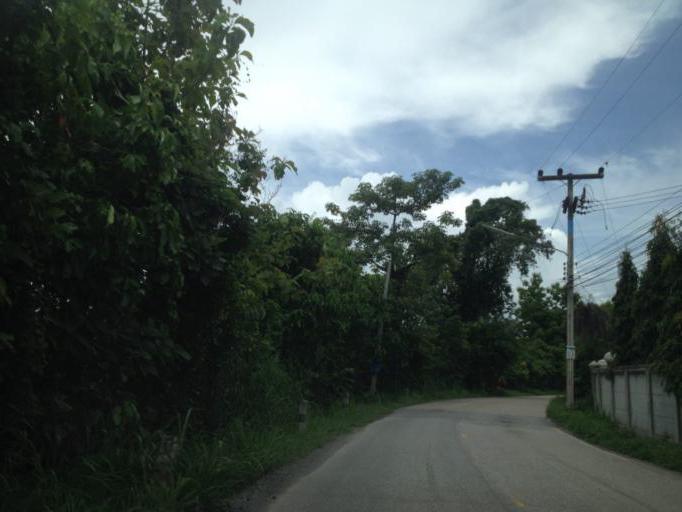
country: TH
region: Chiang Mai
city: Hang Dong
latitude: 18.6867
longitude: 98.8863
